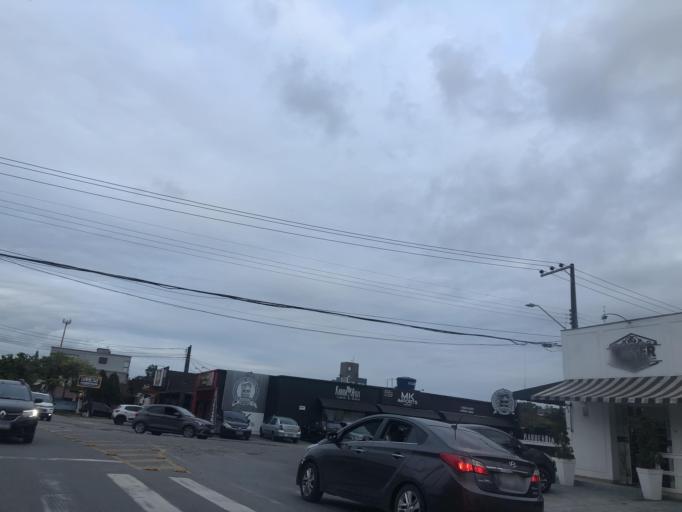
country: BR
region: Santa Catarina
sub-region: Joinville
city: Joinville
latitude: -26.3214
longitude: -48.8328
